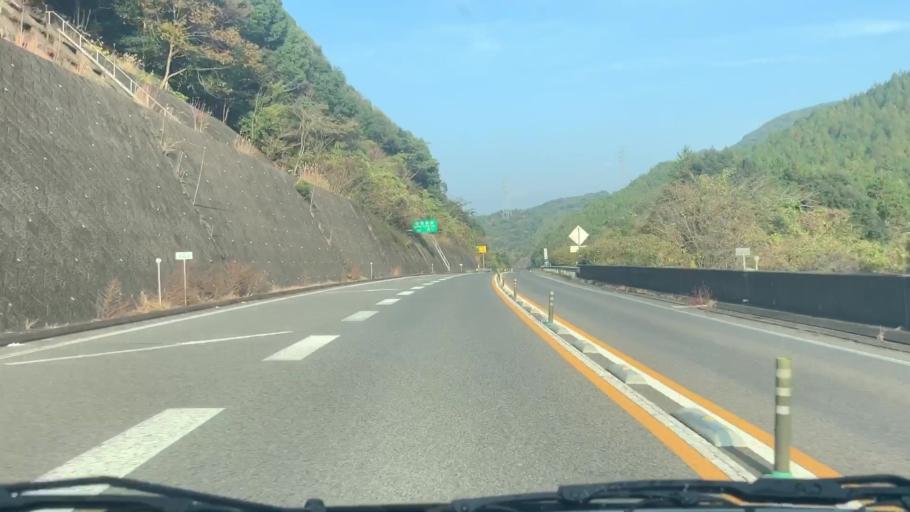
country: JP
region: Saga Prefecture
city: Imaricho-ko
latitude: 33.1610
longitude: 129.8655
